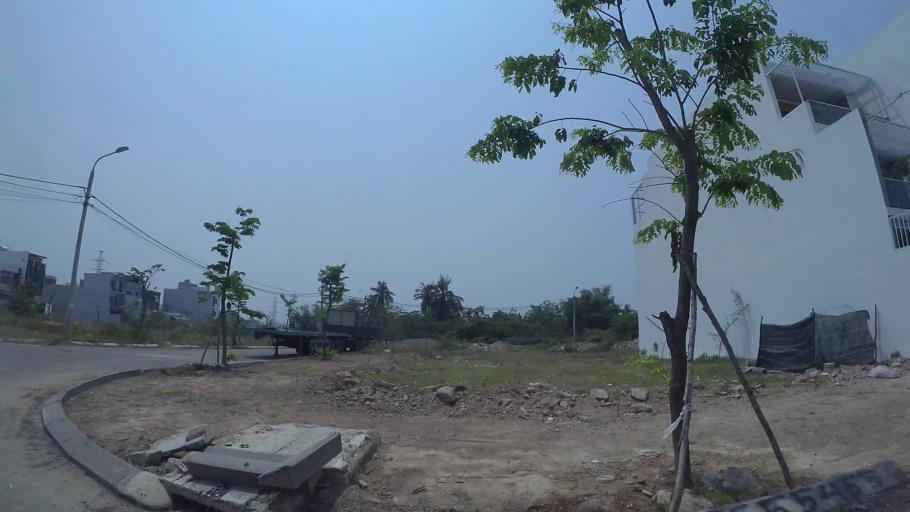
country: VN
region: Da Nang
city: Cam Le
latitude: 16.0186
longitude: 108.2271
